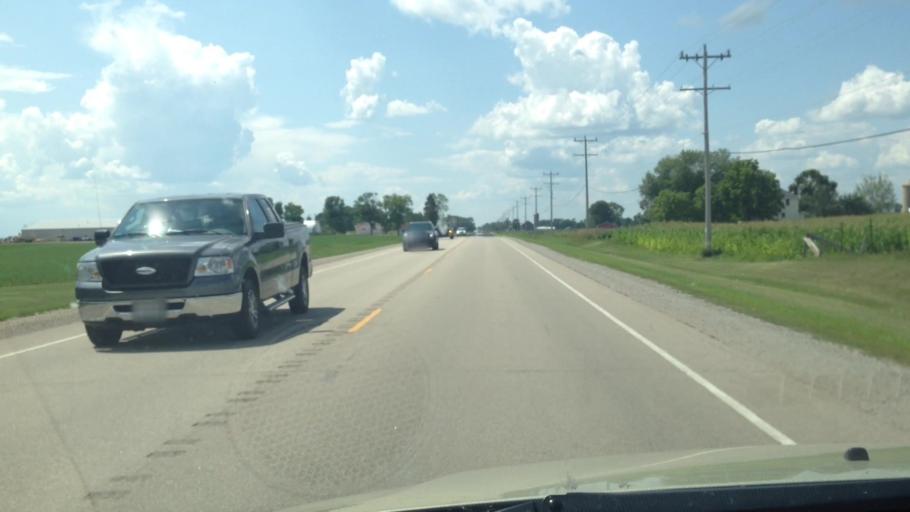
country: US
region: Wisconsin
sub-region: Brown County
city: Pulaski
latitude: 44.6730
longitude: -88.2661
